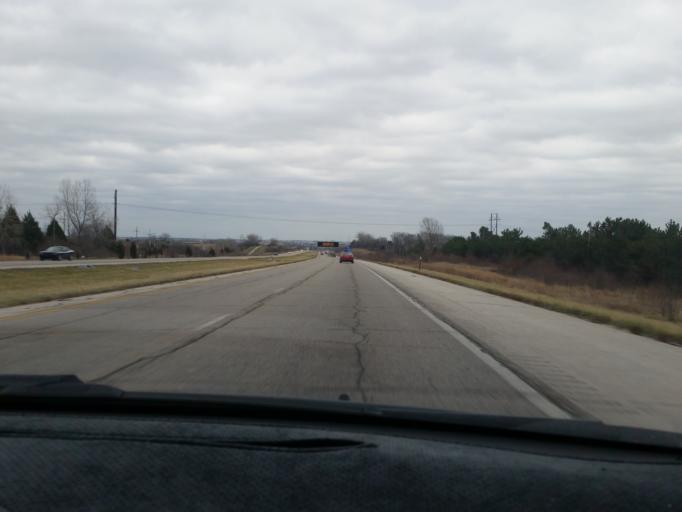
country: US
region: Kansas
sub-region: Johnson County
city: Olathe
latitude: 38.9412
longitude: -94.8318
